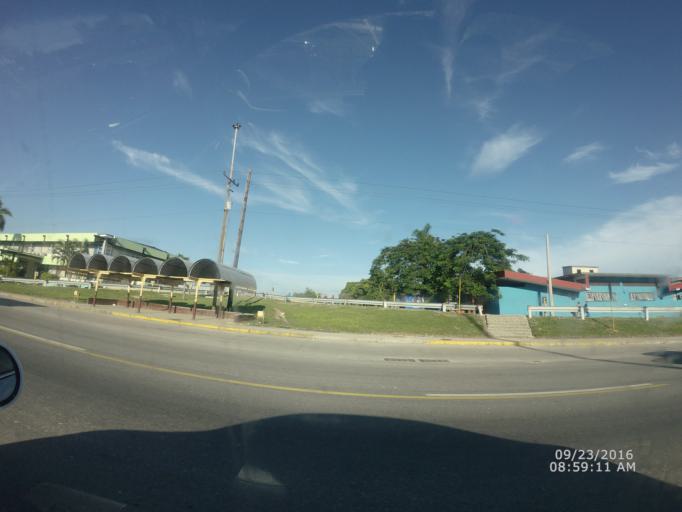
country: CU
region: La Habana
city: Diez de Octubre
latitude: 23.0726
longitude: -82.3978
